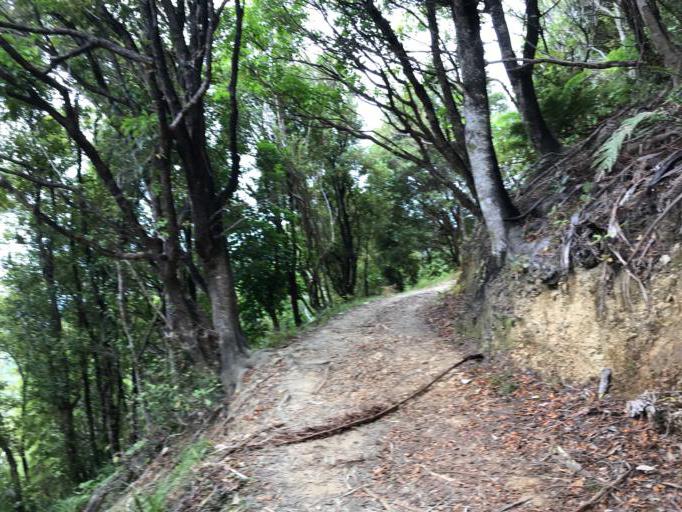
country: NZ
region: Marlborough
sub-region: Marlborough District
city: Picton
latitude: -41.1166
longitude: 174.2040
